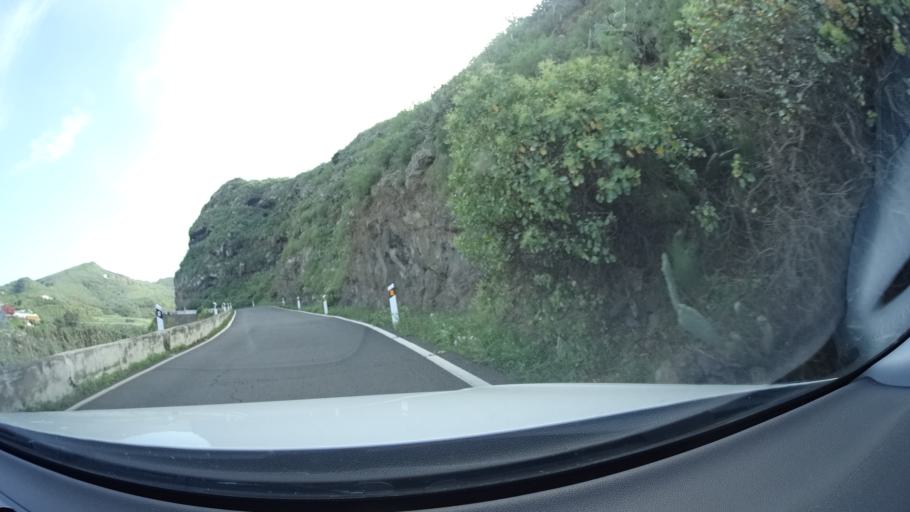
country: ES
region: Canary Islands
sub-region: Provincia de Las Palmas
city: Guia
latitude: 28.1153
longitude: -15.6419
